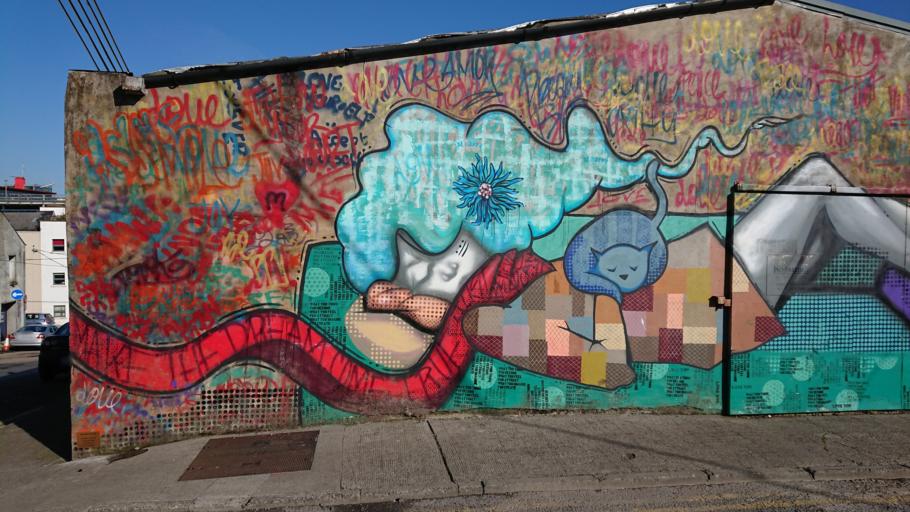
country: IE
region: Munster
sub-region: Waterford
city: Waterford
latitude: 52.2617
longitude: -7.1171
